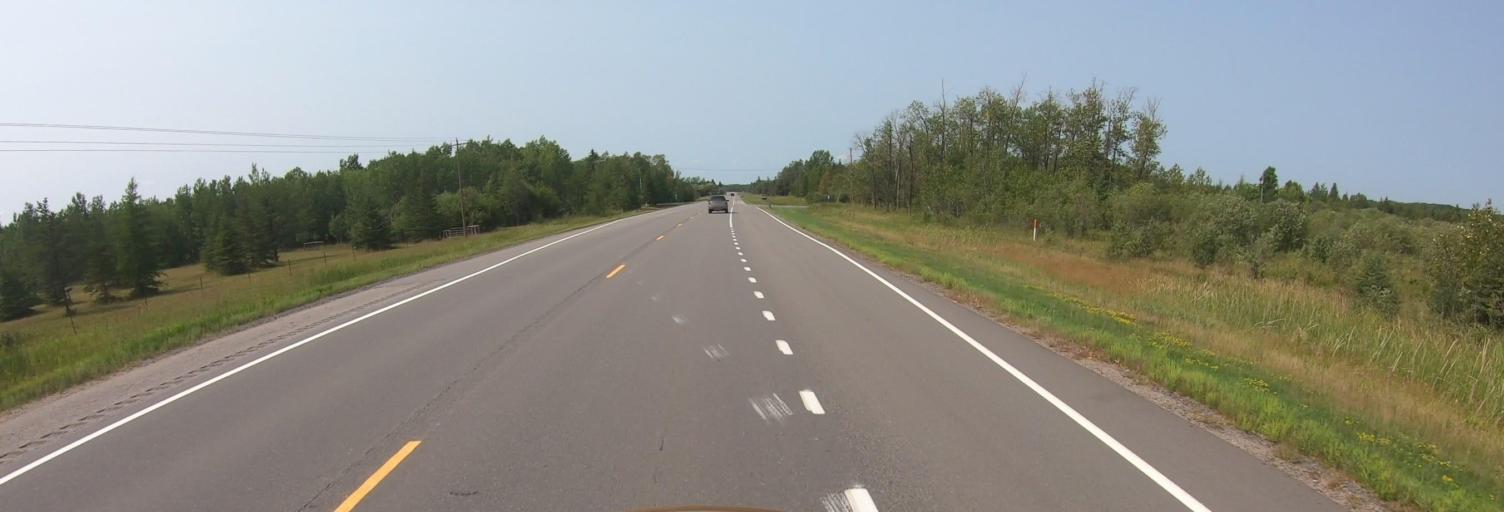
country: US
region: Minnesota
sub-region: Koochiching County
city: International Falls
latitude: 48.5343
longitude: -93.4868
